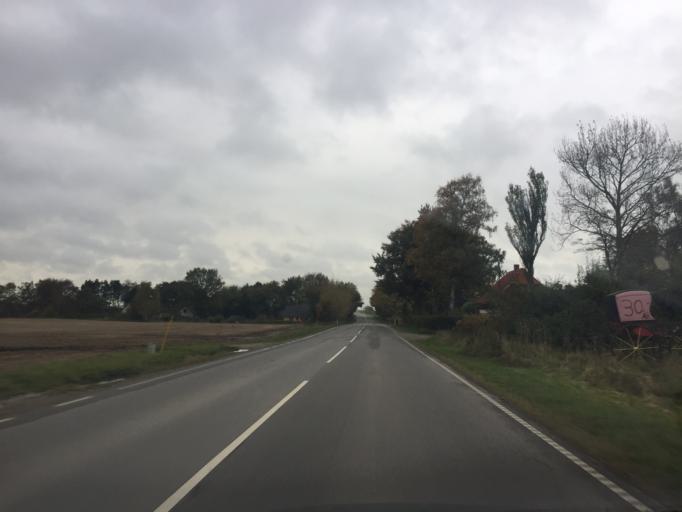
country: DK
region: Capital Region
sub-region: Hoje-Taastrup Kommune
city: Flong
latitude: 55.6675
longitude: 12.2088
